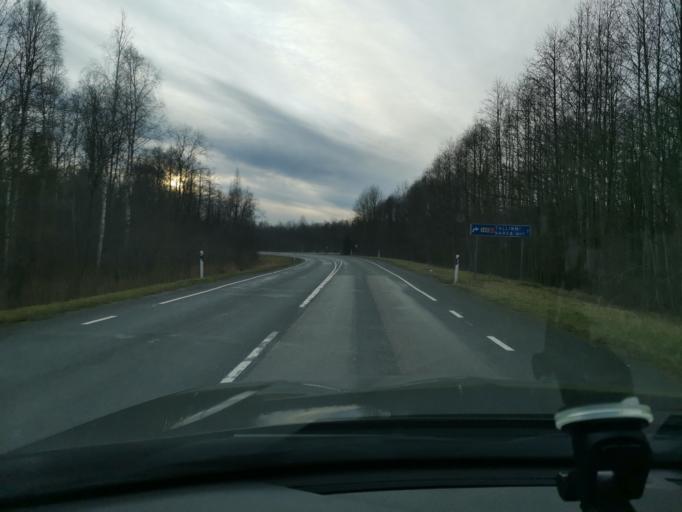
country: EE
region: Ida-Virumaa
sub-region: Sillamaee linn
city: Sillamae
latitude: 59.3243
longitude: 27.9203
